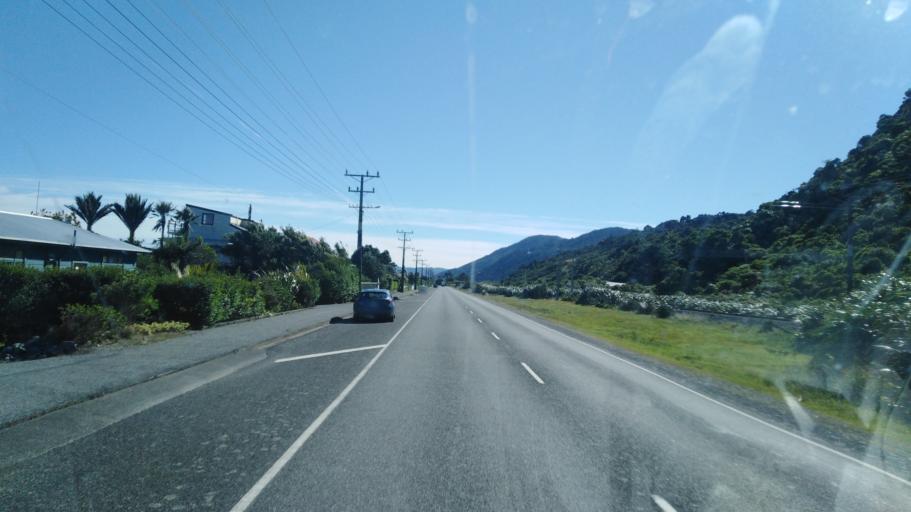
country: NZ
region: West Coast
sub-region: Buller District
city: Westport
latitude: -41.6228
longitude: 171.8604
